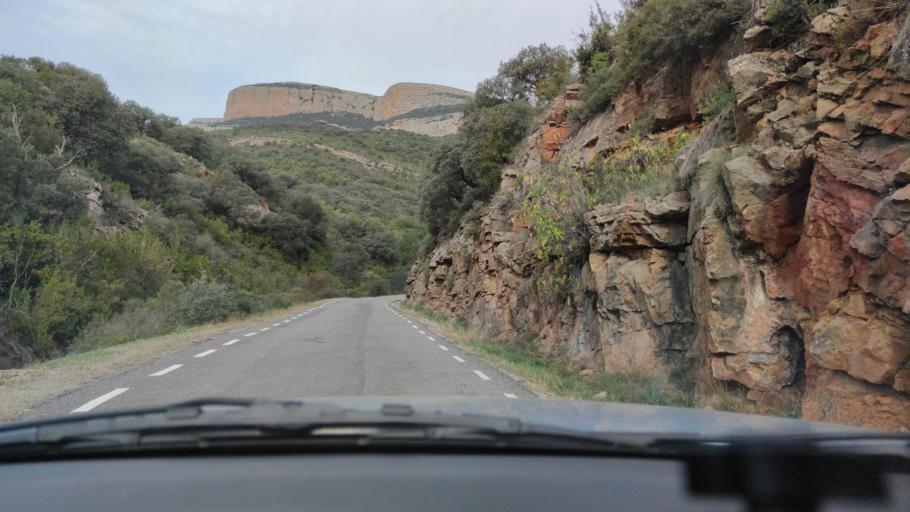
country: ES
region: Catalonia
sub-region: Provincia de Lleida
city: Artesa de Segre
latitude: 42.0122
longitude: 1.0321
